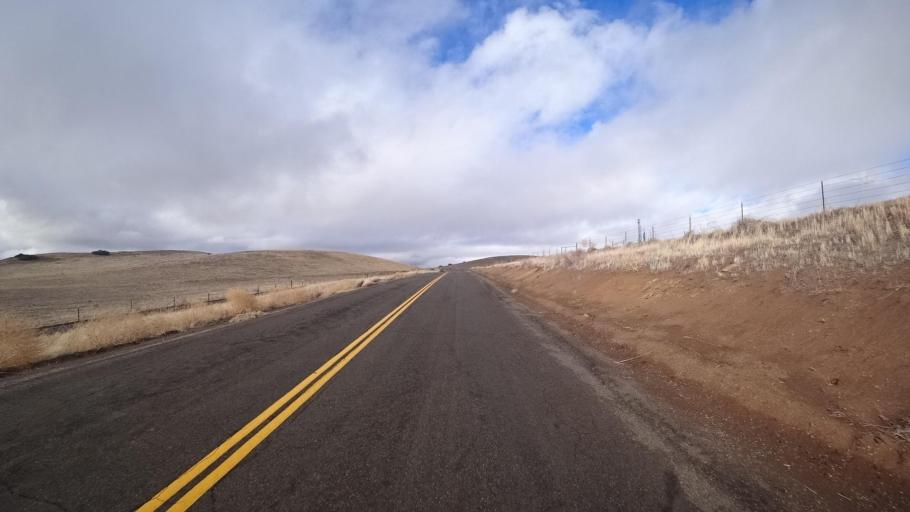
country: US
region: California
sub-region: Kern County
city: Maricopa
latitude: 34.9146
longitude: -119.4018
